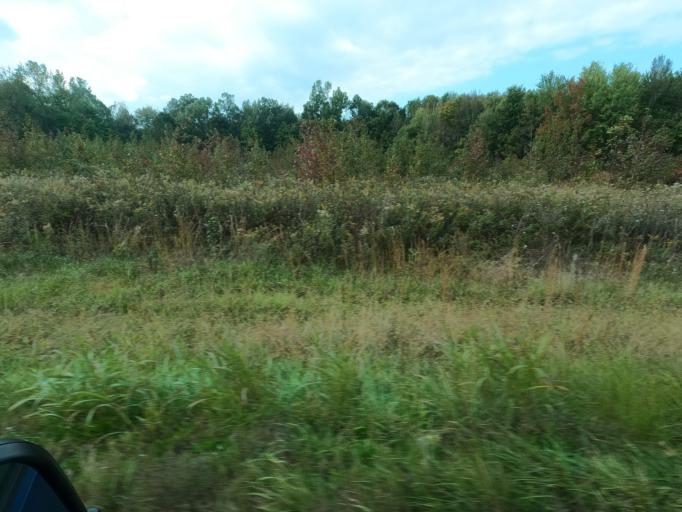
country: US
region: Tennessee
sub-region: Cheatham County
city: Pleasant View
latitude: 36.4465
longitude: -87.1013
